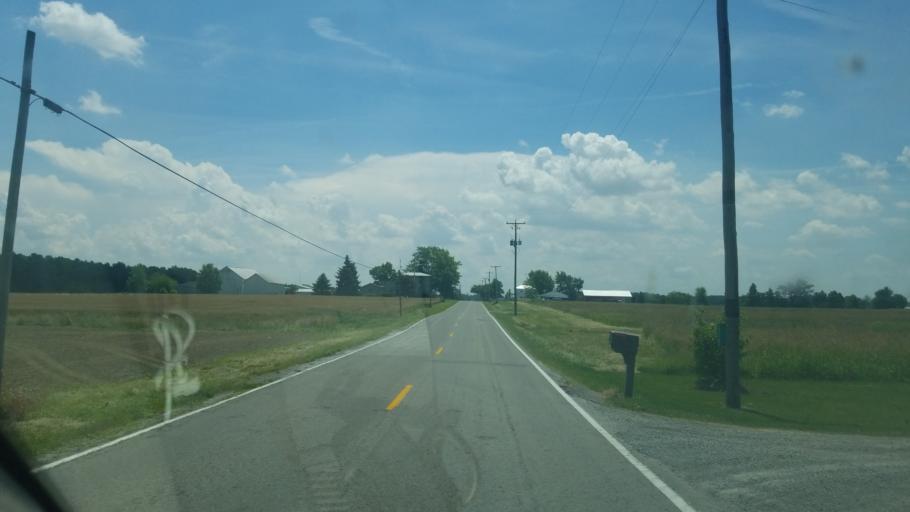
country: US
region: Ohio
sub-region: Hancock County
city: Arlington
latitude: 40.9173
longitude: -83.5946
